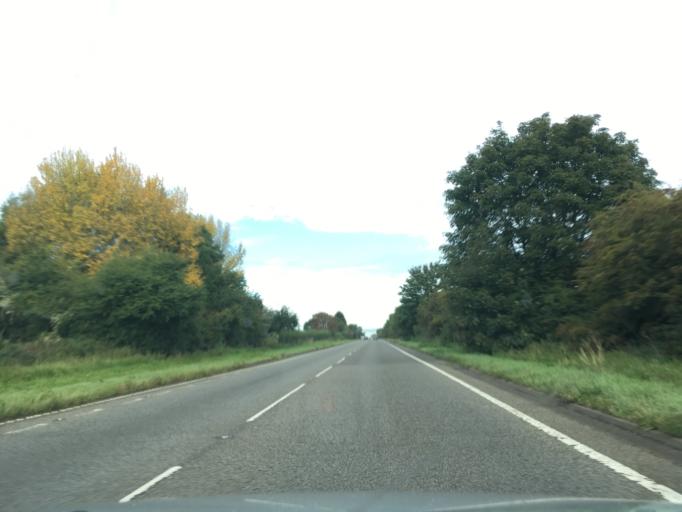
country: GB
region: England
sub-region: Oxfordshire
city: Oxford
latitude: 51.7772
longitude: -1.2335
